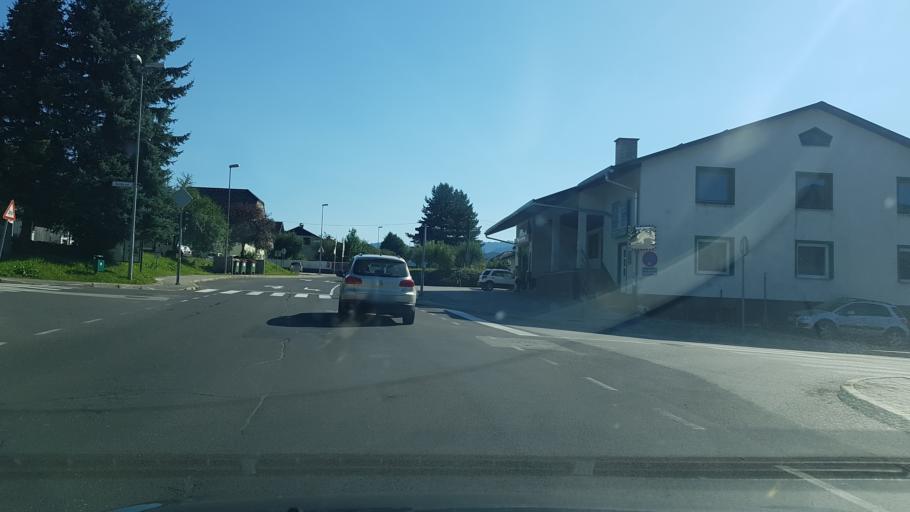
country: SI
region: Slovenj Gradec
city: Slovenj Gradec
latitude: 46.5047
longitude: 15.0748
